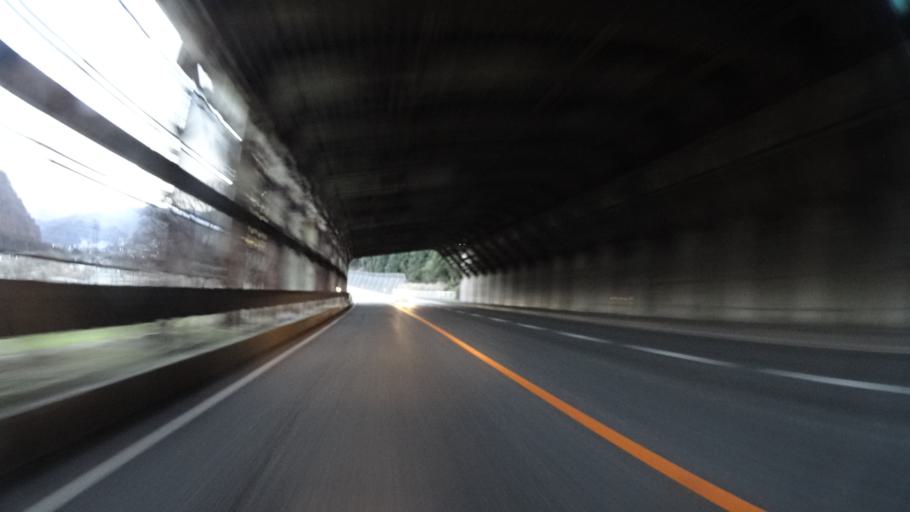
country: JP
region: Niigata
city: Shiozawa
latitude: 36.9599
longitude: 138.7991
